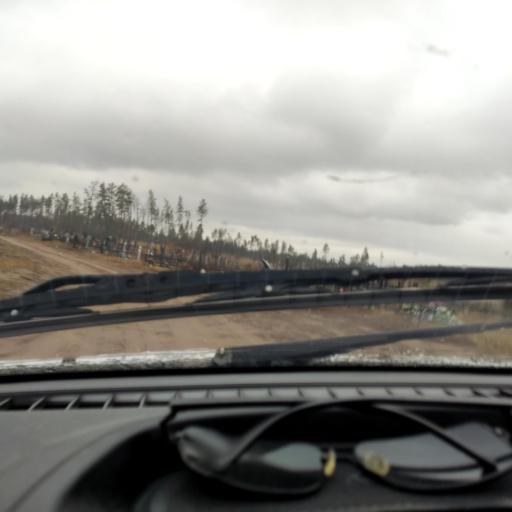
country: RU
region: Samara
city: Zhigulevsk
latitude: 53.5386
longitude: 49.5544
